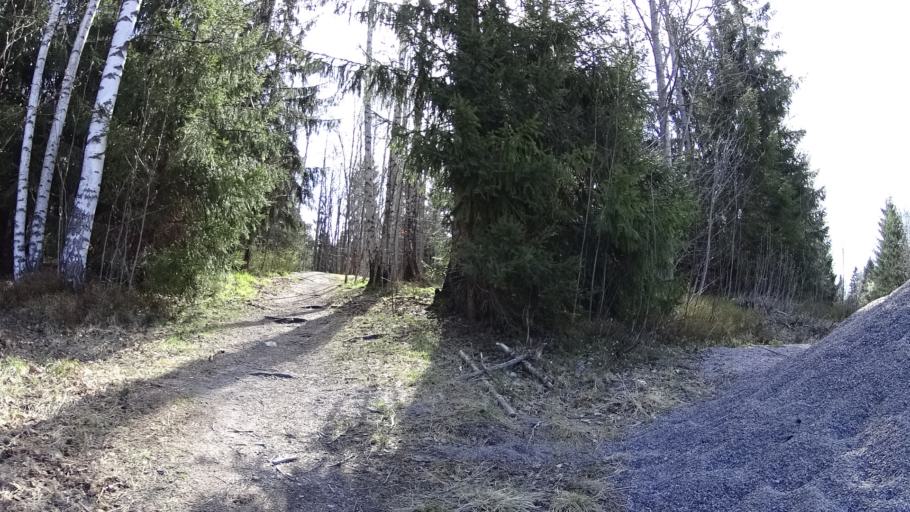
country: FI
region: Uusimaa
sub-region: Helsinki
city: Kilo
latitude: 60.2432
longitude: 24.7837
